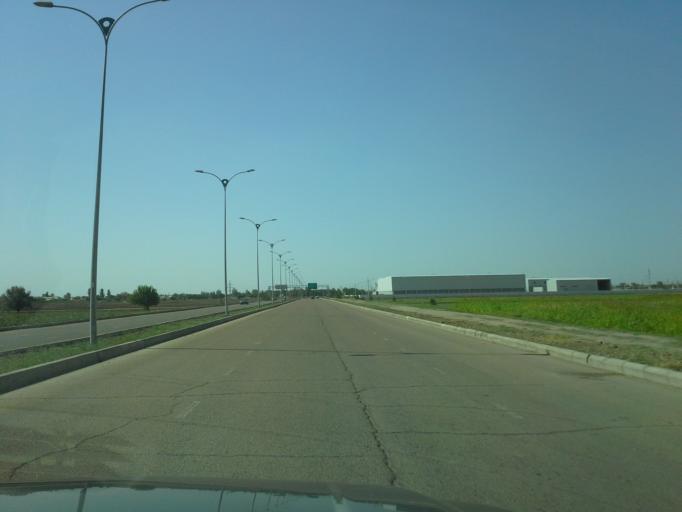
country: TM
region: Dasoguz
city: Dasoguz
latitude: 41.8086
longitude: 60.0016
